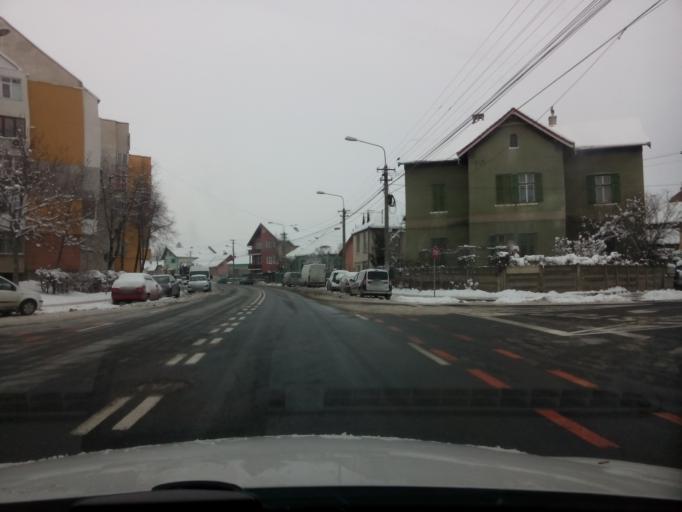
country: RO
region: Sibiu
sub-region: Municipiul Sibiu
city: Sibiu
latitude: 45.8067
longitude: 24.1518
